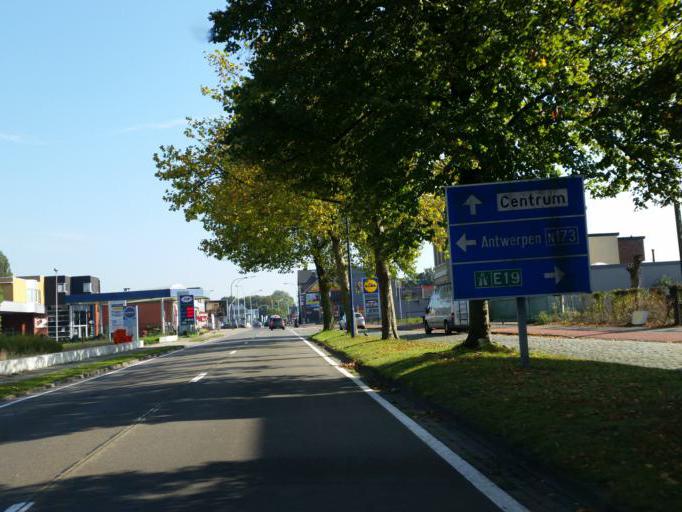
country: BE
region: Flanders
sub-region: Provincie Antwerpen
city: Kontich
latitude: 51.1384
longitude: 4.4359
